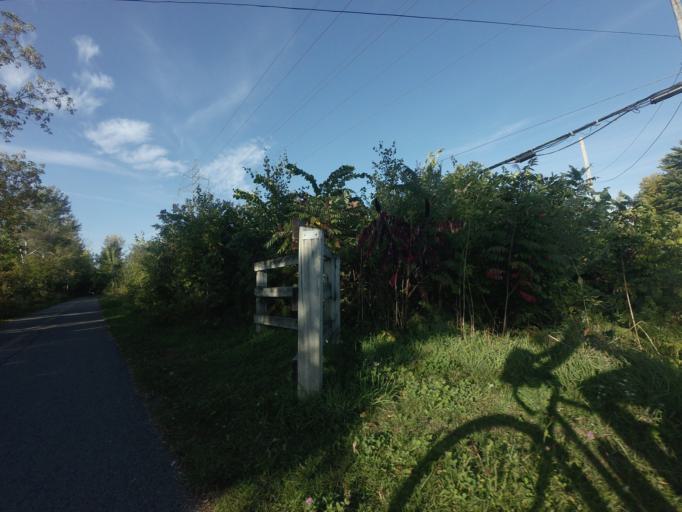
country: CA
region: Quebec
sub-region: Laurentides
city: Saint-Jerome
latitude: 45.7878
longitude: -73.9967
